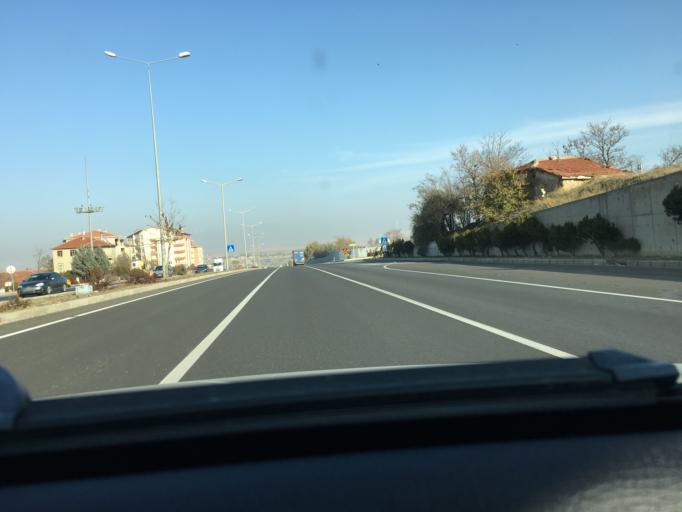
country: TR
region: Ankara
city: Temelli
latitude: 39.7240
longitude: 32.3519
